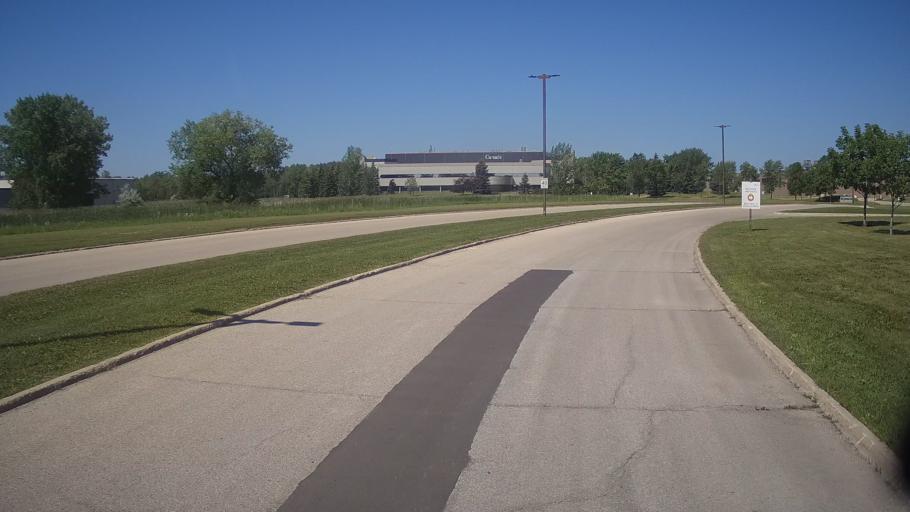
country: CA
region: Manitoba
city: Winnipeg
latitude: 49.8508
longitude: -97.0503
